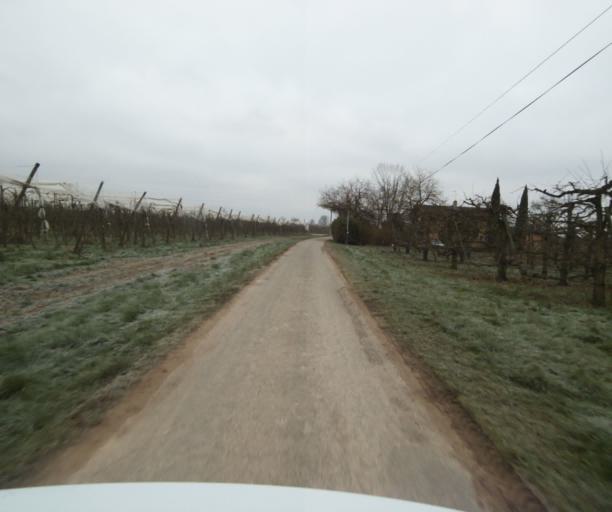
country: FR
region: Midi-Pyrenees
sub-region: Departement du Tarn-et-Garonne
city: Moissac
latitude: 44.1069
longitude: 1.1485
